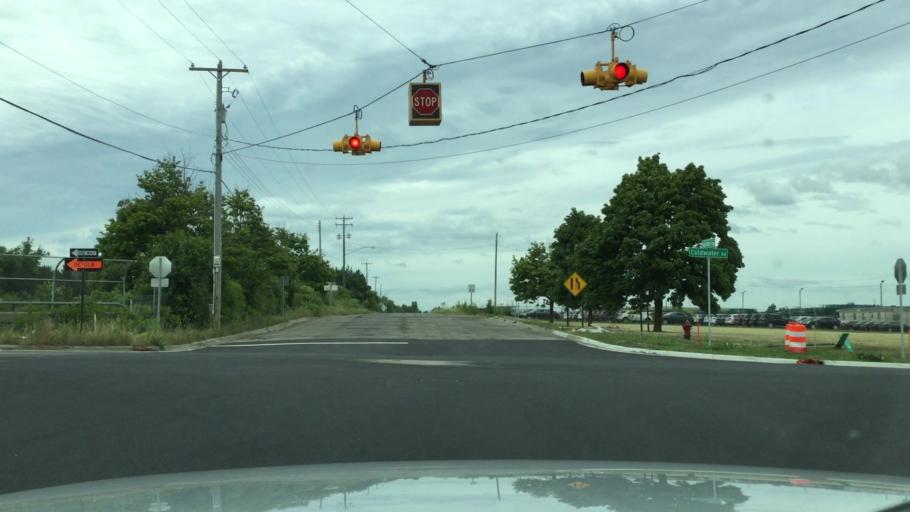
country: US
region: Michigan
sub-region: Genesee County
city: Beecher
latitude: 43.0902
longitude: -83.6861
